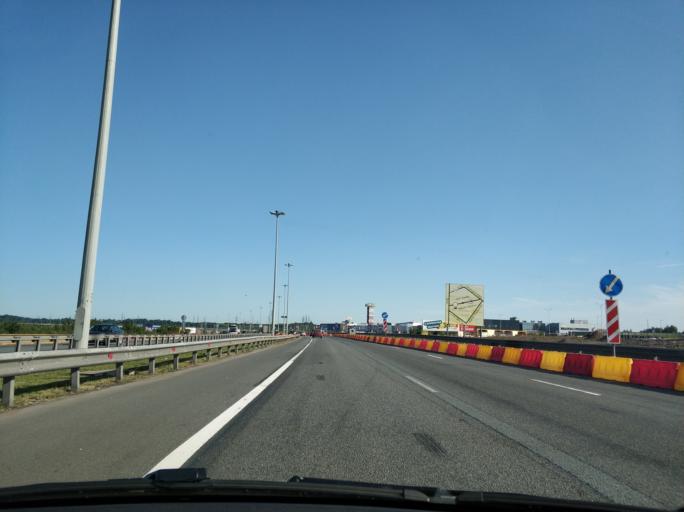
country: RU
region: Leningrad
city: Bugry
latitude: 60.0822
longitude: 30.3792
